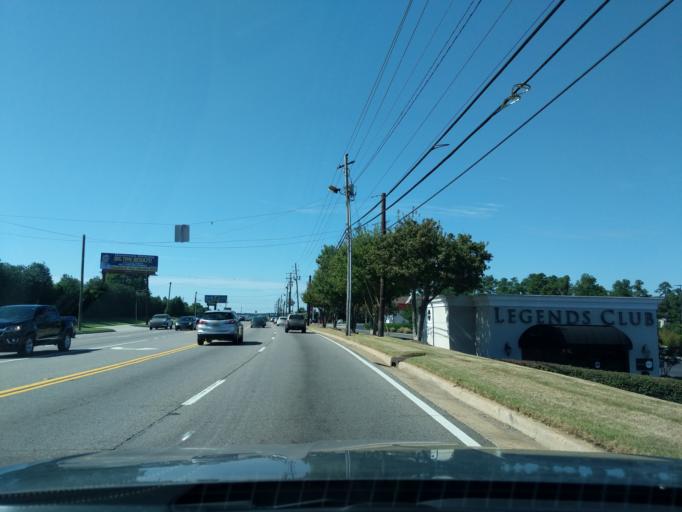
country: US
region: Georgia
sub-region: Columbia County
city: Martinez
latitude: 33.5087
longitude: -82.0230
